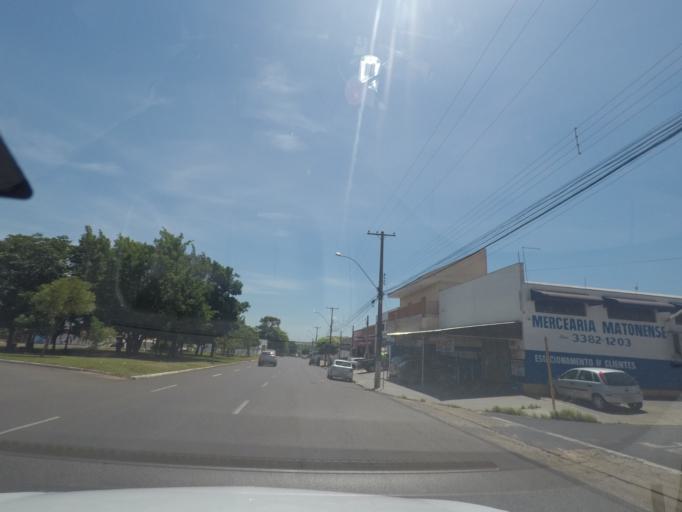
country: BR
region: Sao Paulo
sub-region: Matao
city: Matao
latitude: -21.6161
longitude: -48.3544
